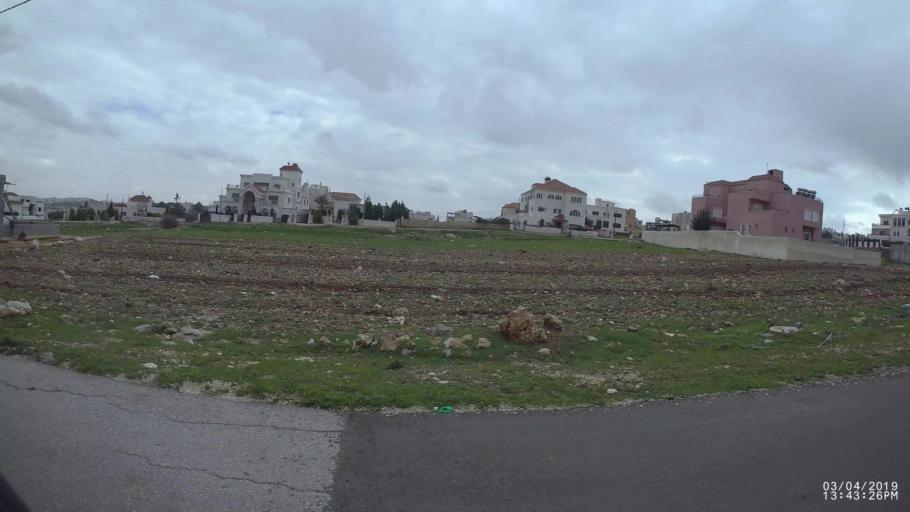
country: JO
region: Amman
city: Umm as Summaq
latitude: 31.9261
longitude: 35.8547
